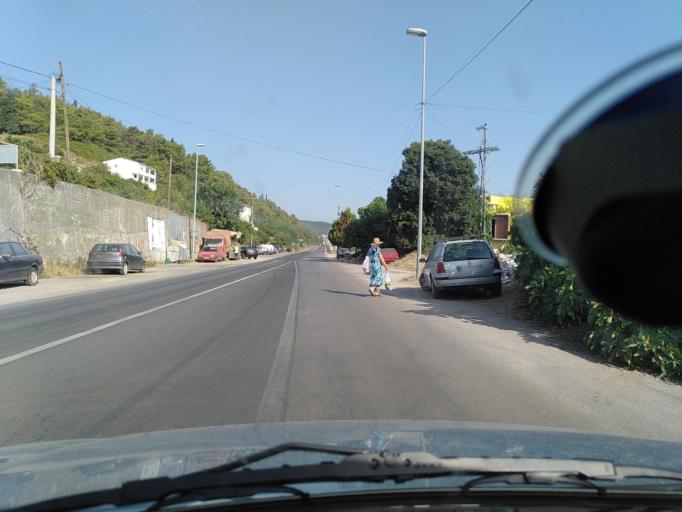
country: ME
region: Ulcinj
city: Ulcinj
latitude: 41.9378
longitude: 19.2181
